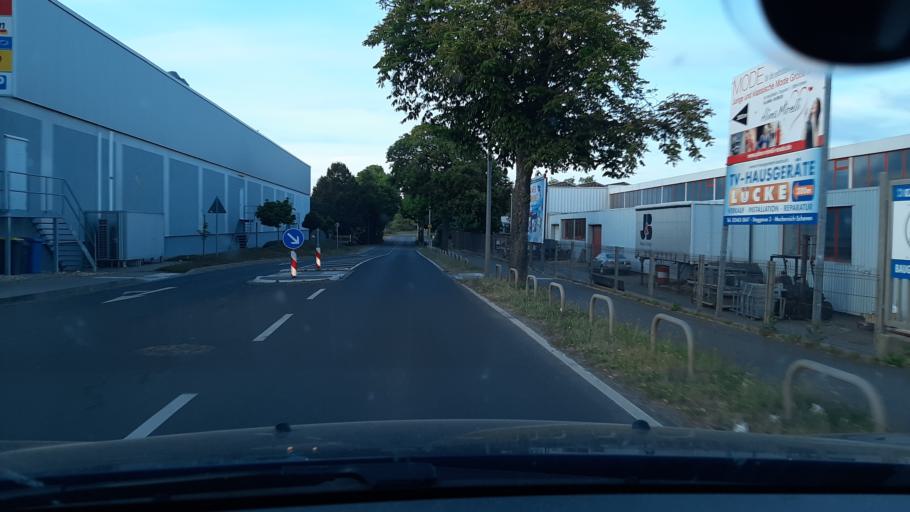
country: DE
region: North Rhine-Westphalia
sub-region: Regierungsbezirk Koln
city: Mechernich
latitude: 50.6178
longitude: 6.6575
